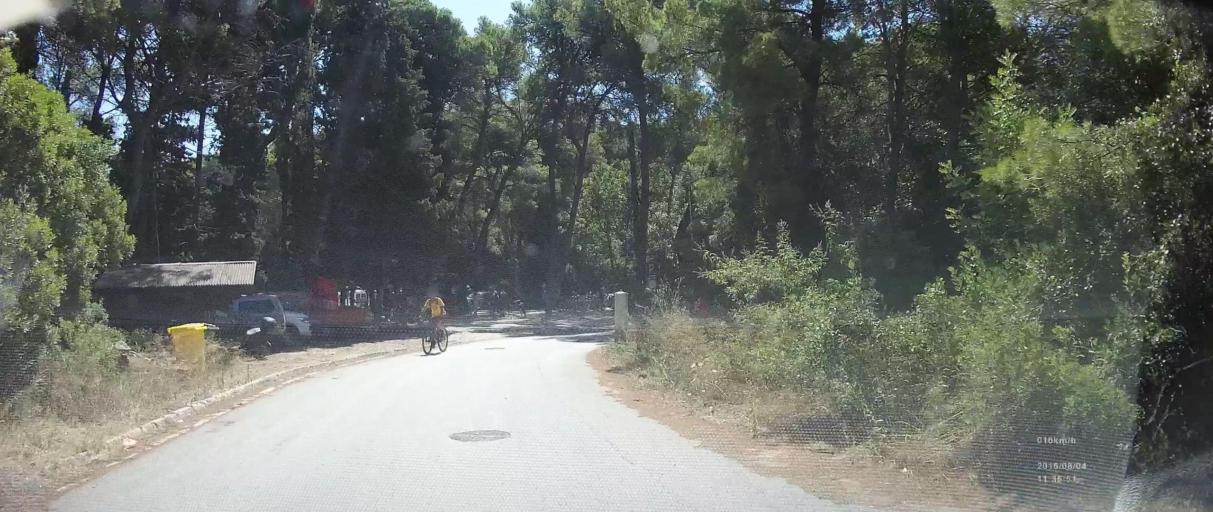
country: HR
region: Dubrovacko-Neretvanska
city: Blato
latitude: 42.7787
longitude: 17.3675
